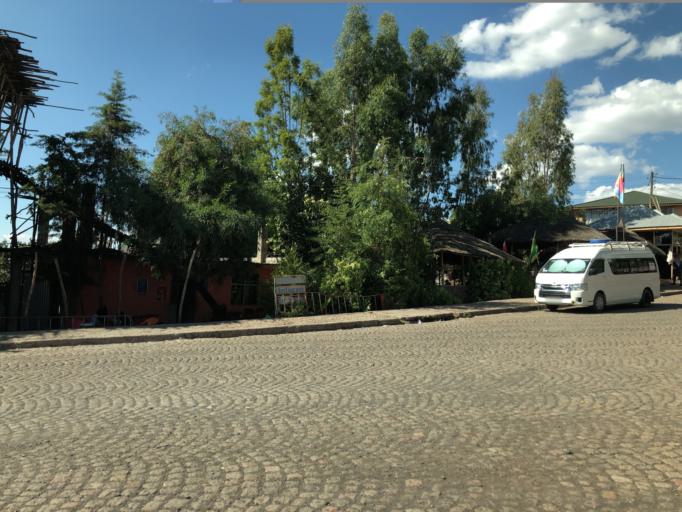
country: ET
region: Amhara
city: Lalibela
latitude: 12.0282
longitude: 39.0424
